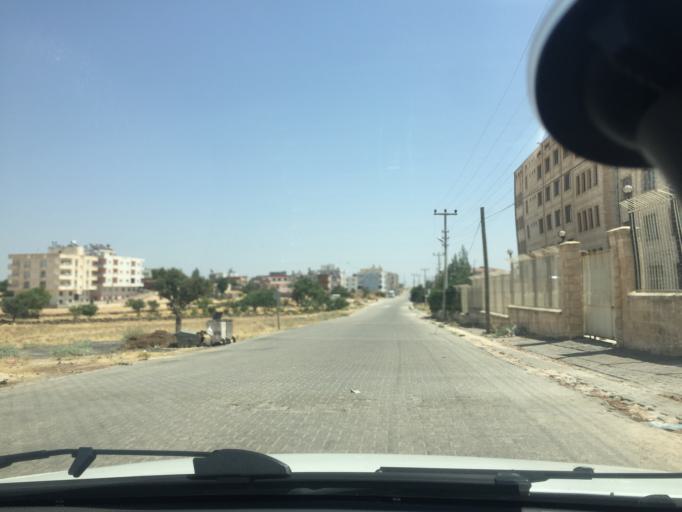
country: TR
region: Mardin
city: Midyat
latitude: 37.4293
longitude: 41.3451
